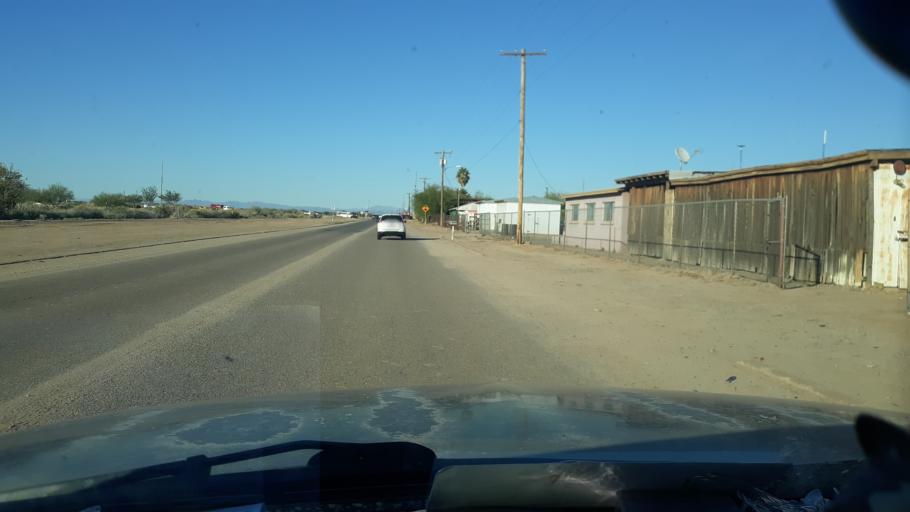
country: US
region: Arizona
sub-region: Maricopa County
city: Citrus Park
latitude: 33.5635
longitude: -112.3936
